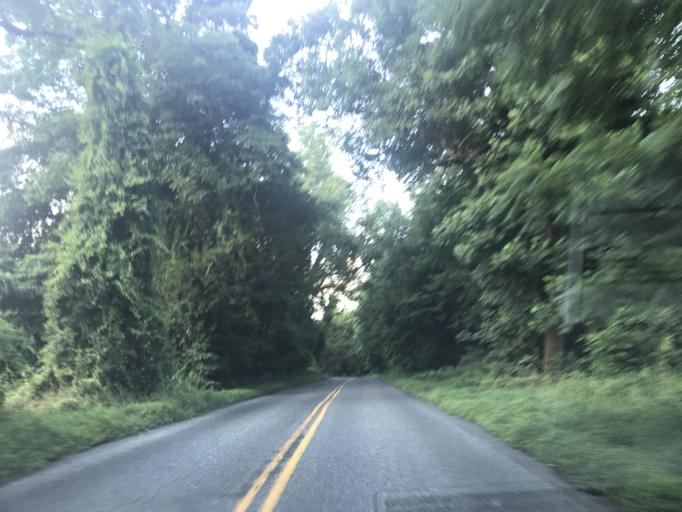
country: US
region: Maryland
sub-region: Cecil County
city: Rising Sun
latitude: 39.6504
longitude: -76.1782
